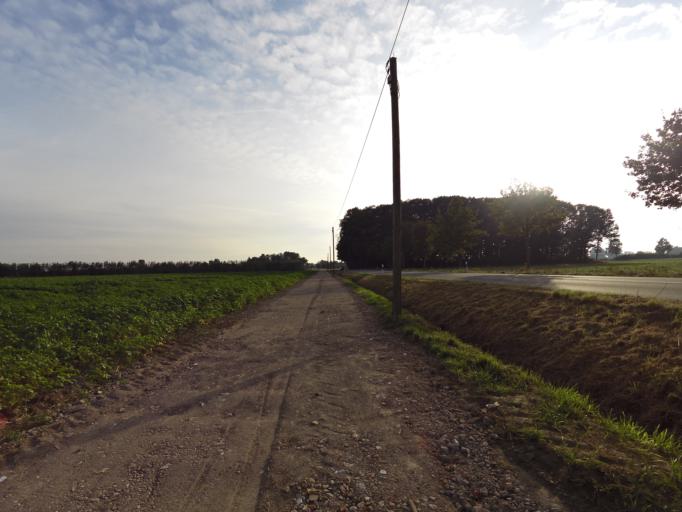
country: DE
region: North Rhine-Westphalia
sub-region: Regierungsbezirk Dusseldorf
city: Bocholt
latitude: 51.8004
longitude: 6.5599
